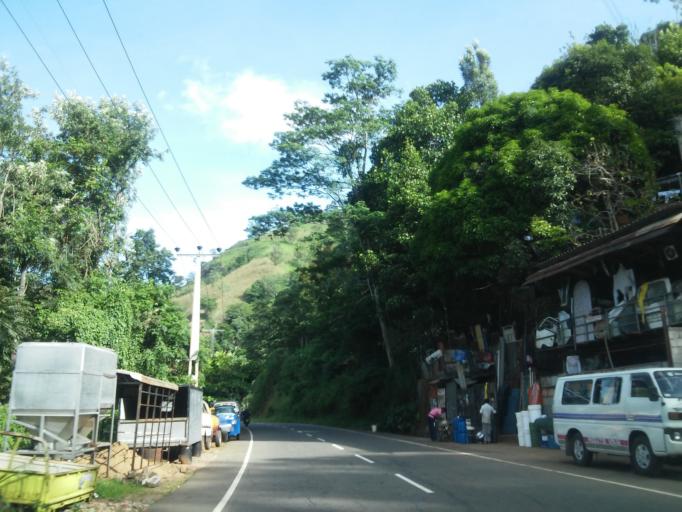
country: LK
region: Uva
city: Haputale
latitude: 6.7641
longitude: 80.8990
